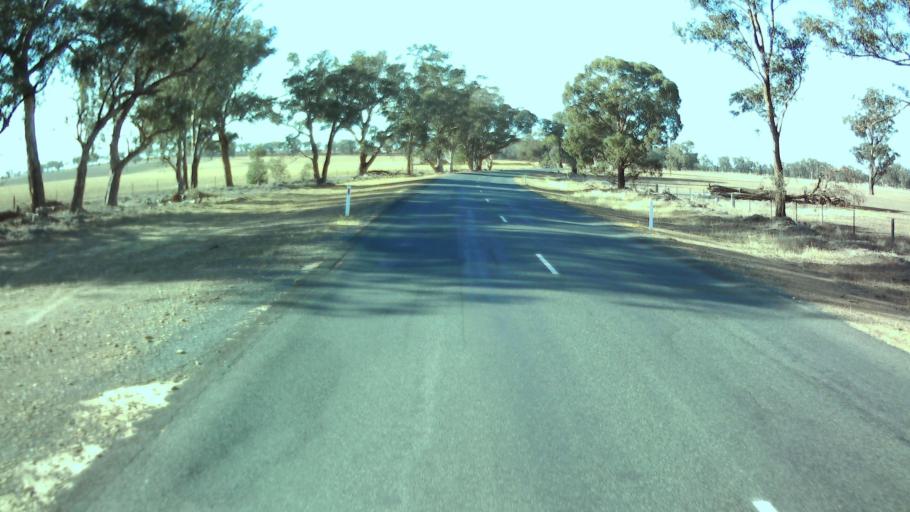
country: AU
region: New South Wales
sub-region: Weddin
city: Grenfell
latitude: -33.9338
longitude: 148.1377
